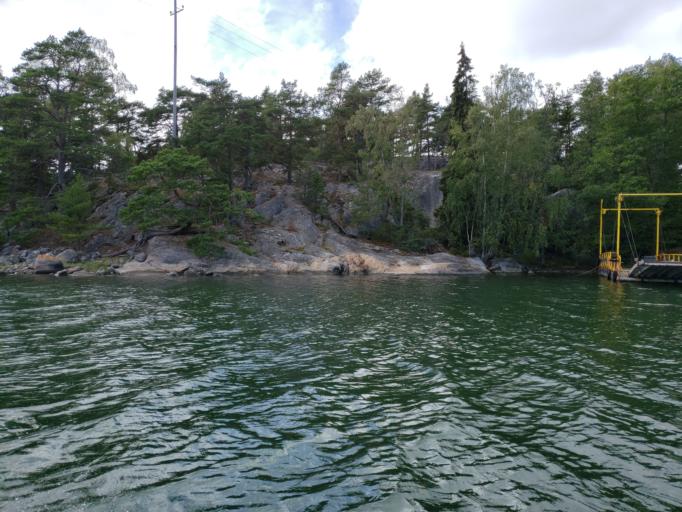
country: FI
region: Varsinais-Suomi
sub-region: Aboland-Turunmaa
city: Dragsfjaerd
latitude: 59.9140
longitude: 22.3792
